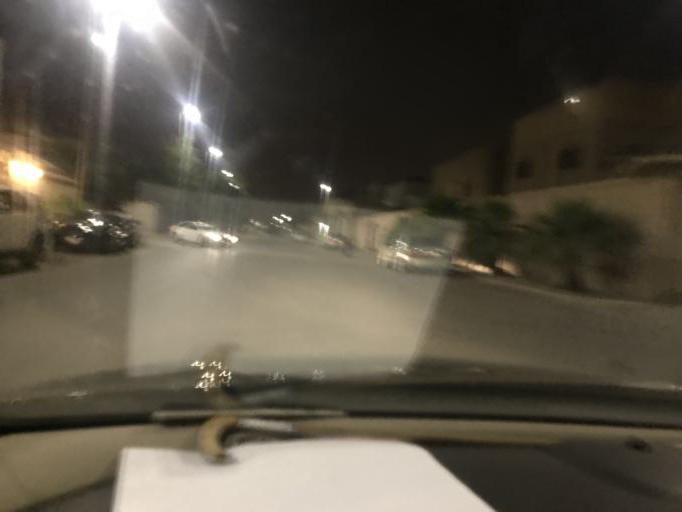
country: SA
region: Ar Riyad
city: Riyadh
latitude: 24.7245
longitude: 46.7734
